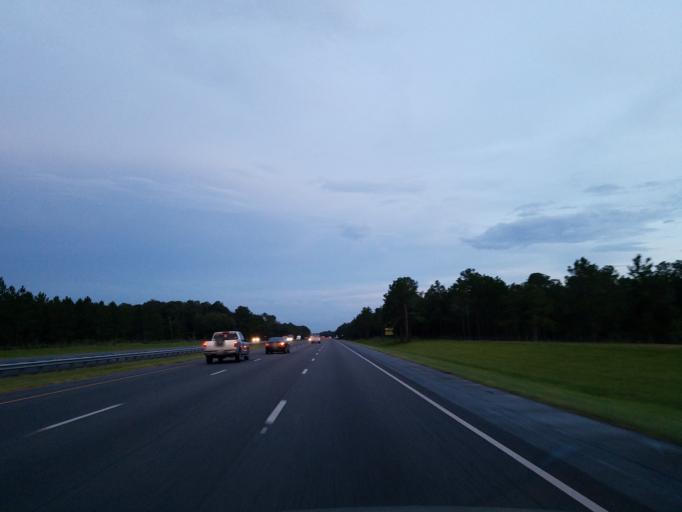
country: US
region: Georgia
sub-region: Lowndes County
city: Valdosta
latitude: 30.7337
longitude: -83.2647
